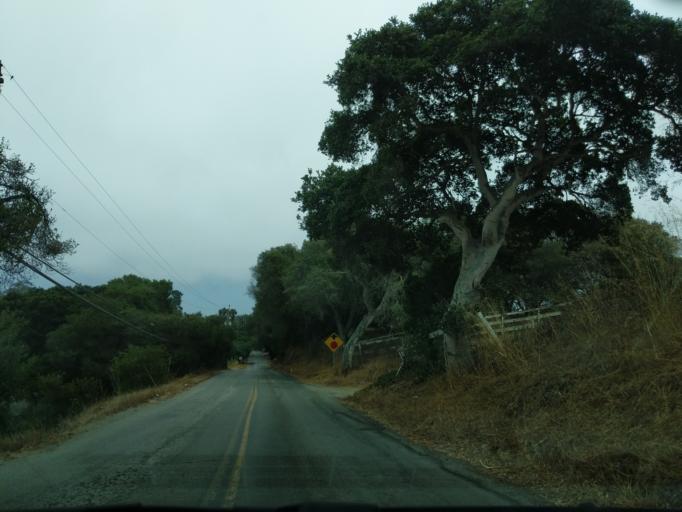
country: US
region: California
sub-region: Monterey County
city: Prunedale
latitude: 36.7885
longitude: -121.6851
